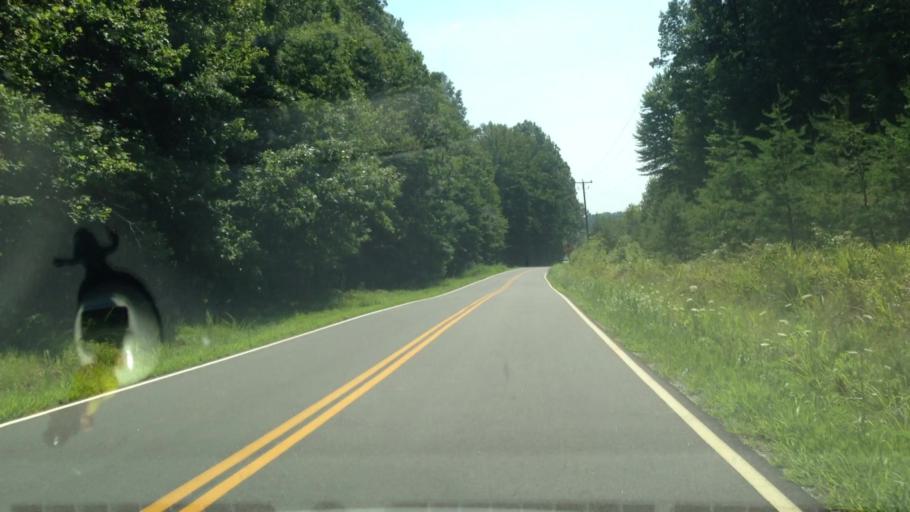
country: US
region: Virginia
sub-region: Patrick County
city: Patrick Springs
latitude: 36.6021
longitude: -80.1646
